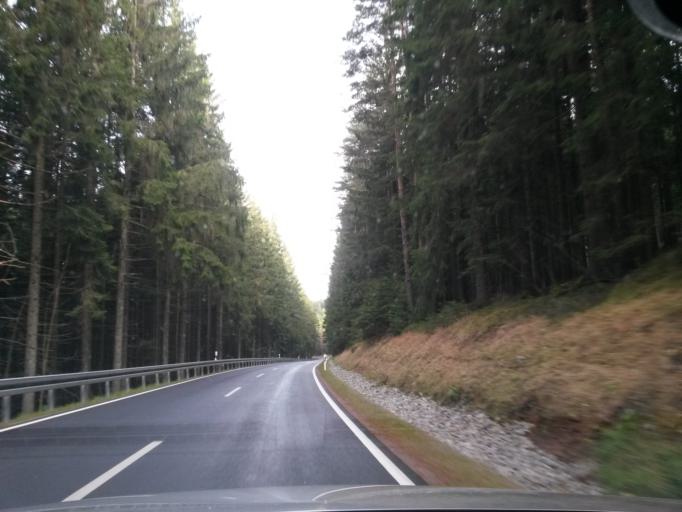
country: DE
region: Baden-Wuerttemberg
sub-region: Freiburg Region
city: Sankt Georgen im Schwarzwald
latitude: 48.1479
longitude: 8.3294
